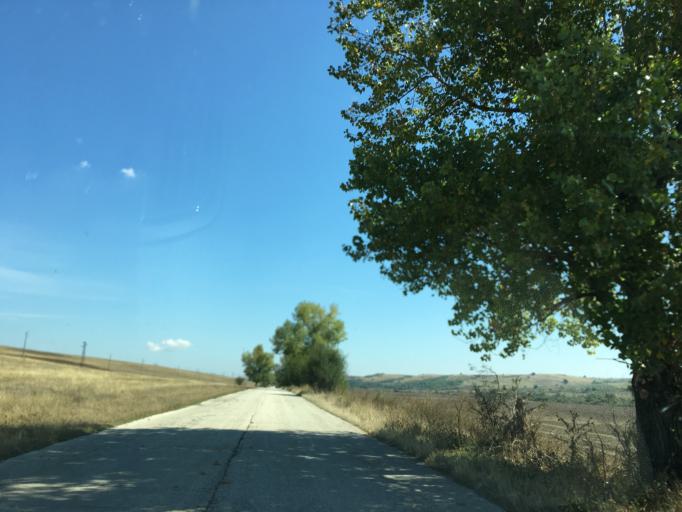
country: BG
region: Pleven
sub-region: Obshtina Knezha
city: Knezha
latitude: 43.5388
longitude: 24.1284
